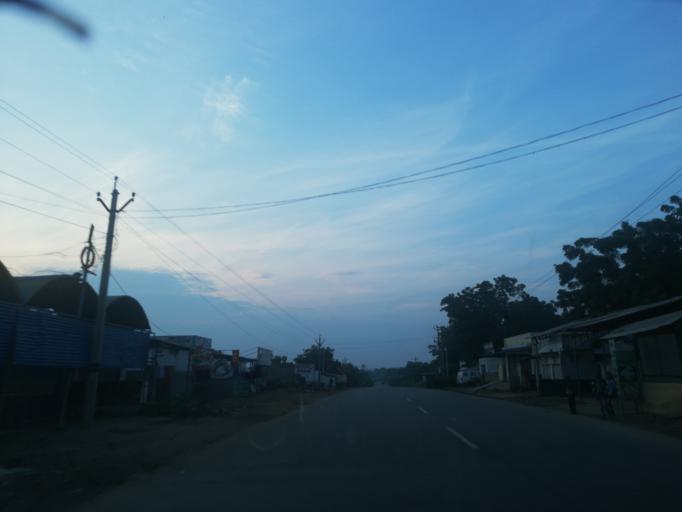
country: IN
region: Andhra Pradesh
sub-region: Guntur
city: Macherla
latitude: 16.5916
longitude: 79.3167
